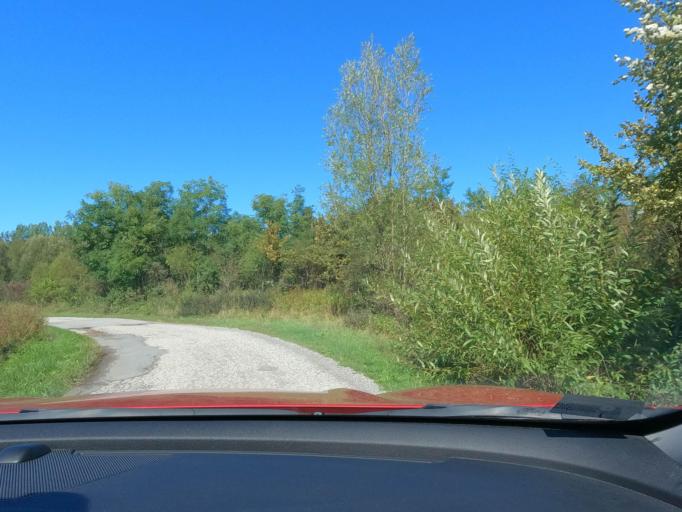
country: HR
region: Sisacko-Moslavacka
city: Petrinja
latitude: 45.3297
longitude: 16.2237
